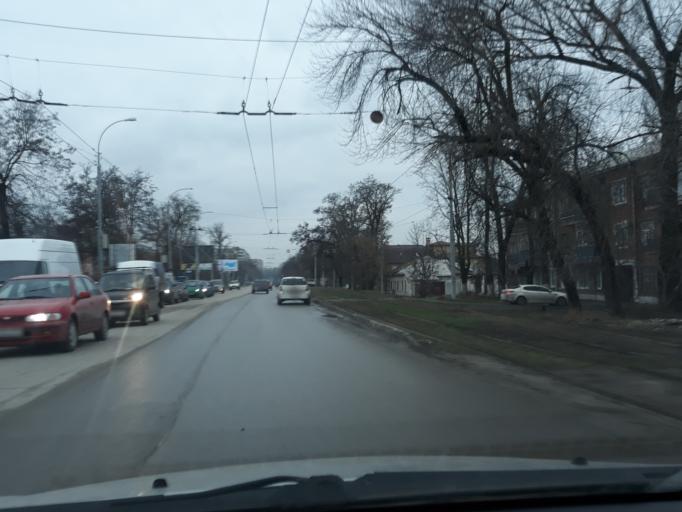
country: RU
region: Rostov
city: Taganrog
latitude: 47.2232
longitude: 38.9169
